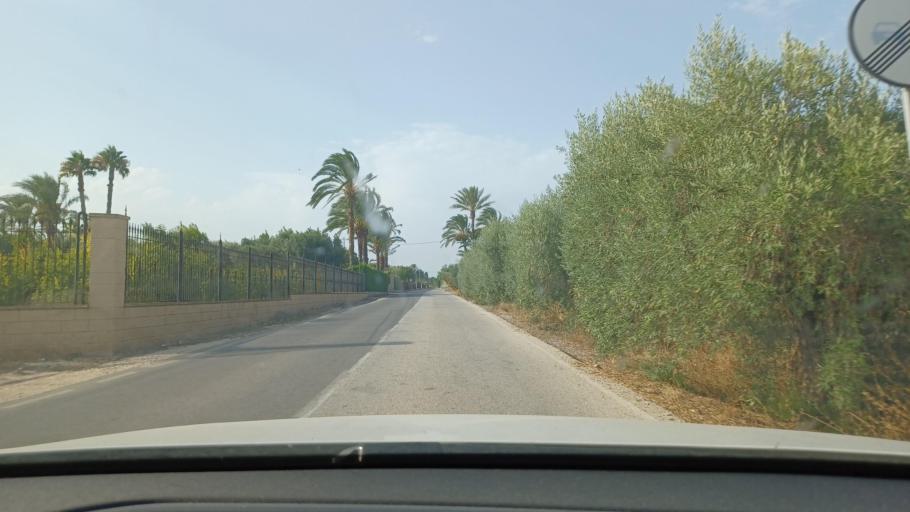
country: ES
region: Valencia
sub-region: Provincia de Alicante
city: Elche
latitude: 38.2307
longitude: -0.6938
